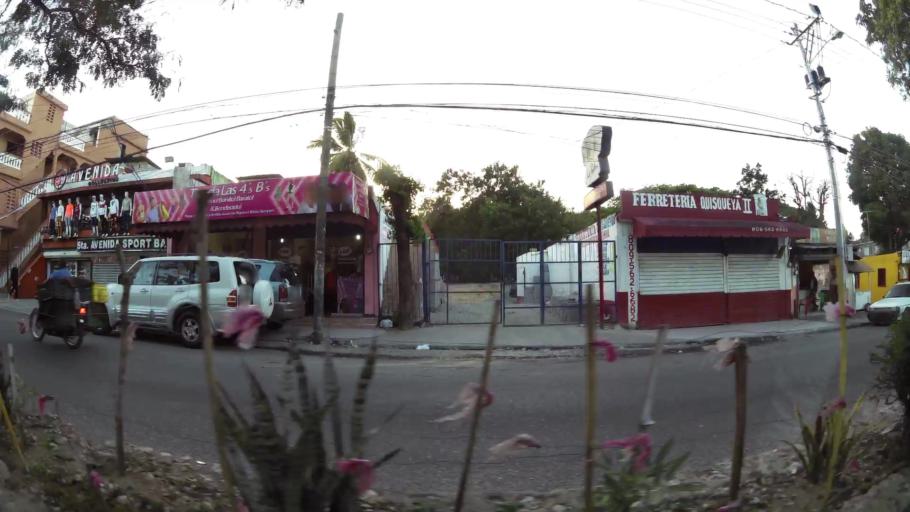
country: DO
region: Nacional
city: Santo Domingo
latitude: 18.4971
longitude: -69.9636
